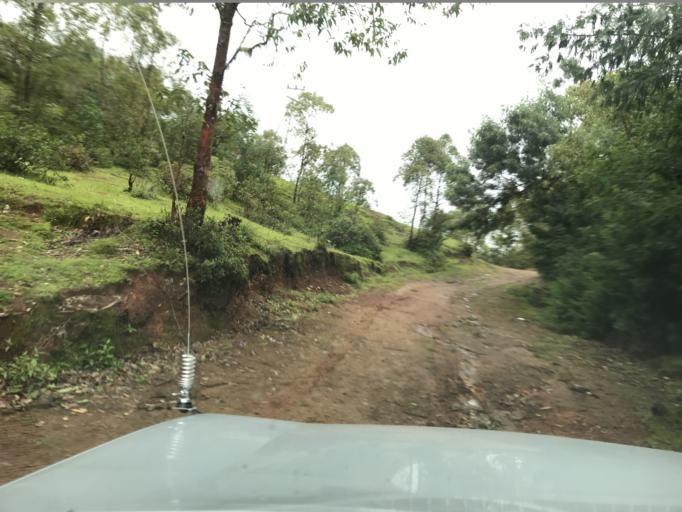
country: TL
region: Ainaro
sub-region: Ainaro
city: Ainaro
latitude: -8.8779
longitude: 125.5536
